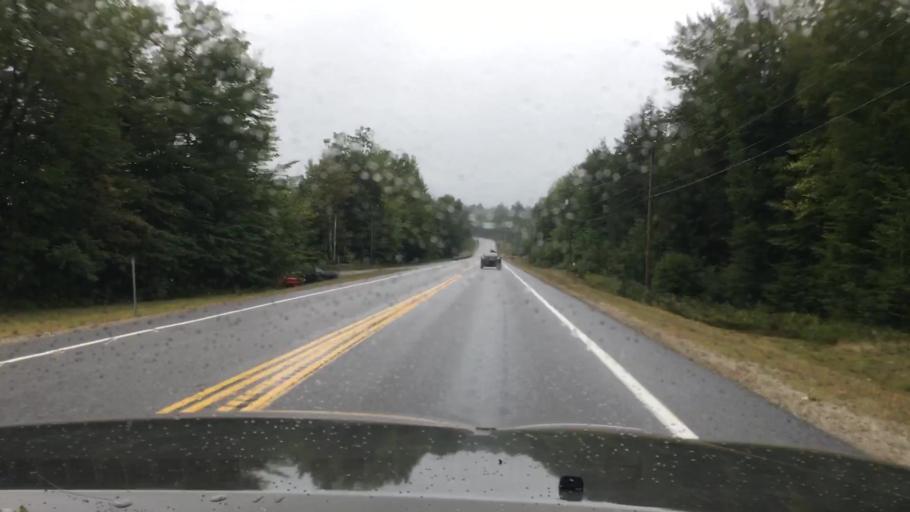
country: US
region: New Hampshire
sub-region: Cheshire County
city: Harrisville
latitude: 43.0539
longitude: -72.0781
